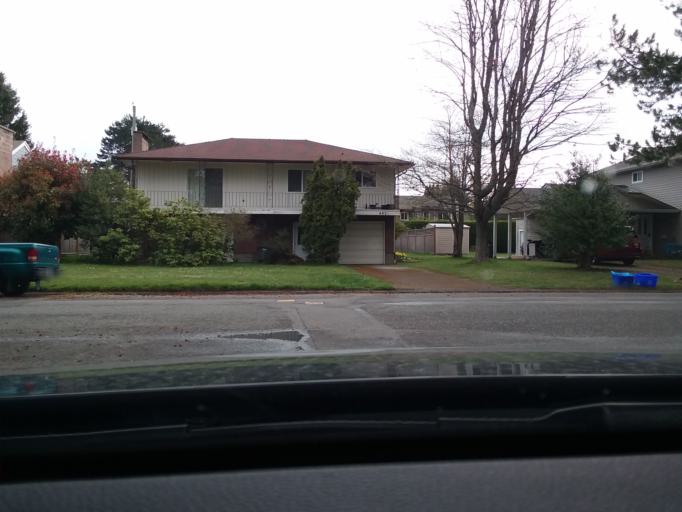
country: CA
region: British Columbia
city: Oak Bay
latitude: 48.4742
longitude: -123.3301
